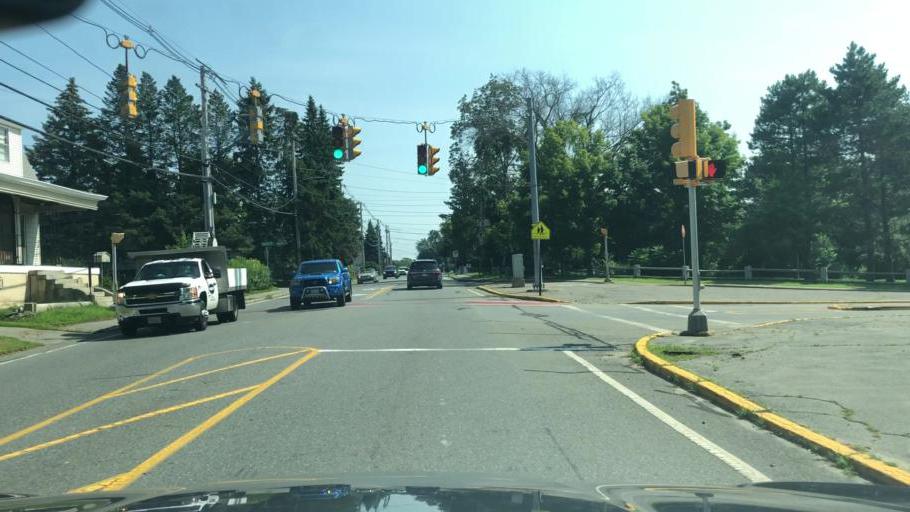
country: US
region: Massachusetts
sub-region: Essex County
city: Methuen
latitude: 42.7486
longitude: -71.1722
